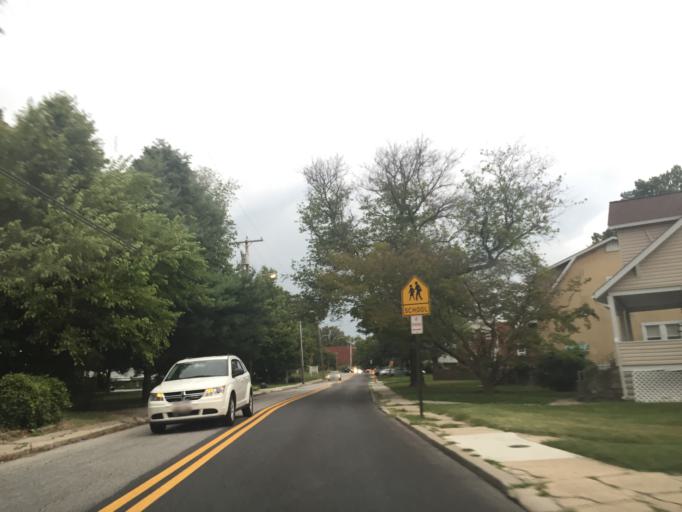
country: US
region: Maryland
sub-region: Baltimore County
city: Parkville
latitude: 39.3629
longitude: -76.5586
